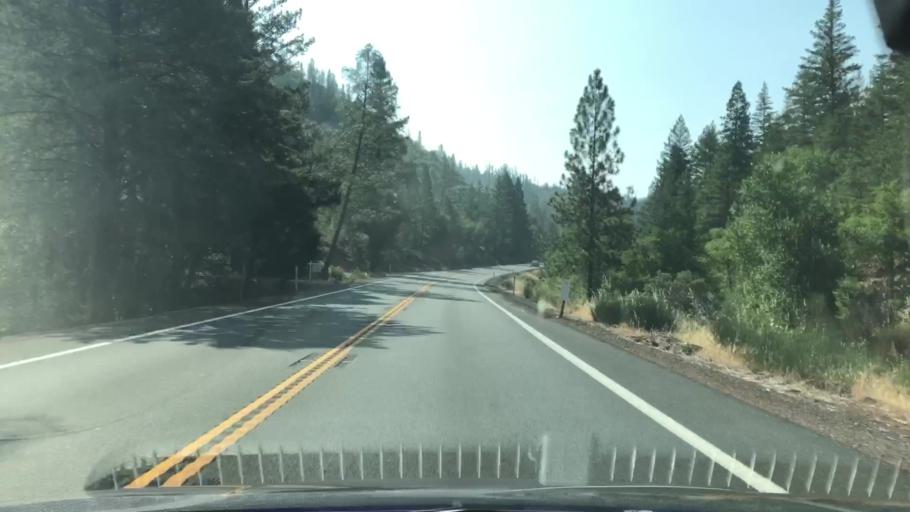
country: US
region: California
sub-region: Lake County
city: Middletown
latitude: 38.6847
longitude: -122.5938
